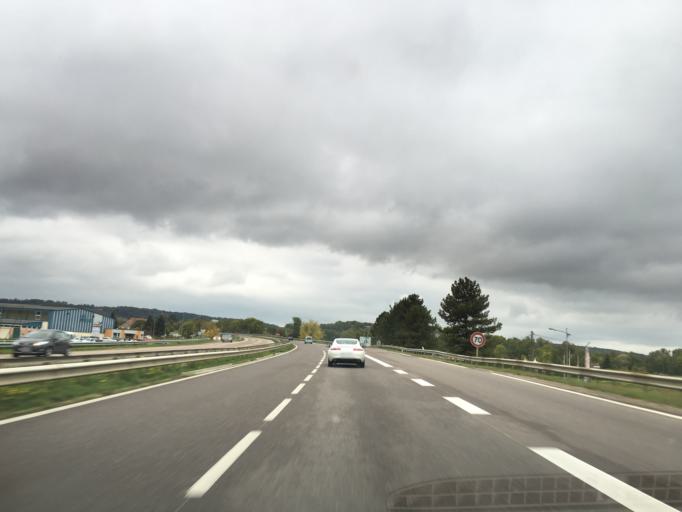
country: FR
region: Lorraine
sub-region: Departement de la Meuse
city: Vacon
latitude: 48.6901
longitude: 5.6265
